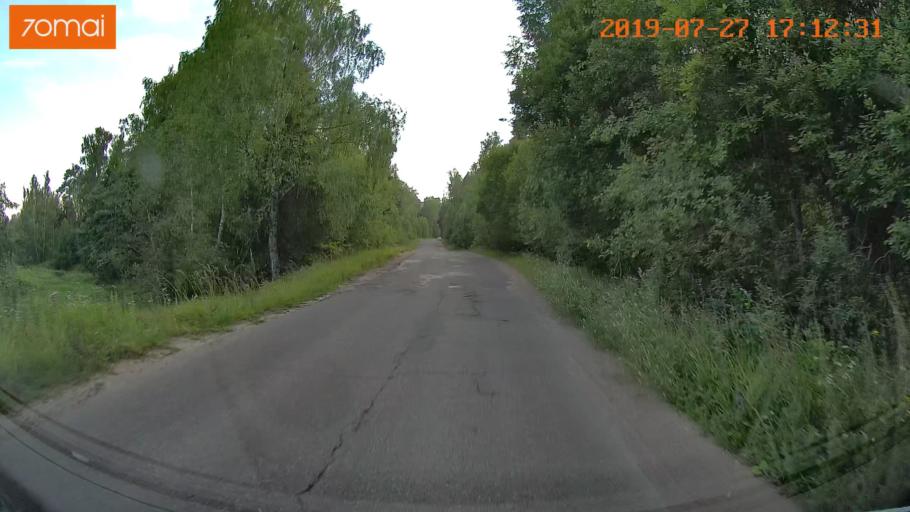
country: RU
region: Ivanovo
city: Novo-Talitsy
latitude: 57.0578
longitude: 40.8610
